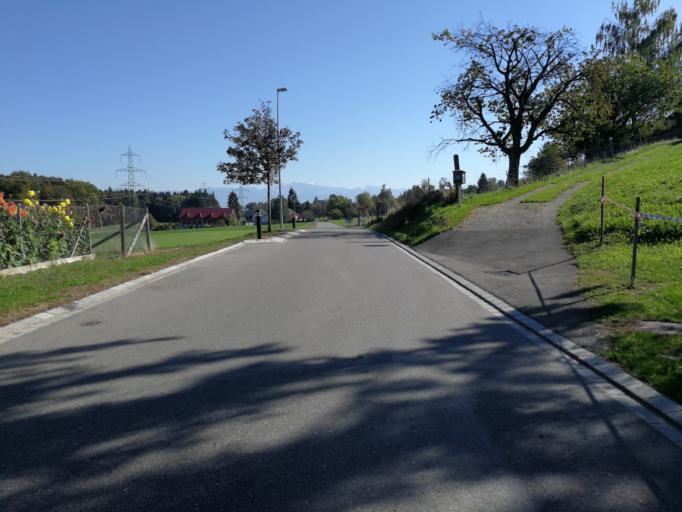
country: CH
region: Zurich
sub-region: Bezirk Uster
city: Aesch
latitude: 47.3218
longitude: 8.6693
